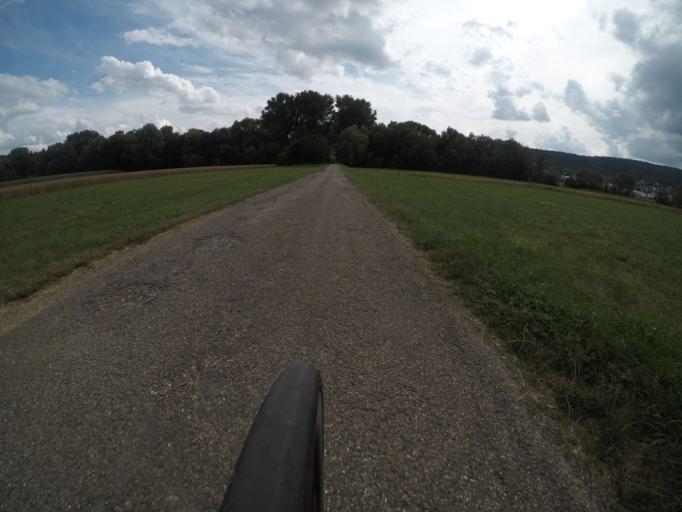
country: DE
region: Baden-Wuerttemberg
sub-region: Regierungsbezirk Stuttgart
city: Weil der Stadt
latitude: 48.7638
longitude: 8.8651
